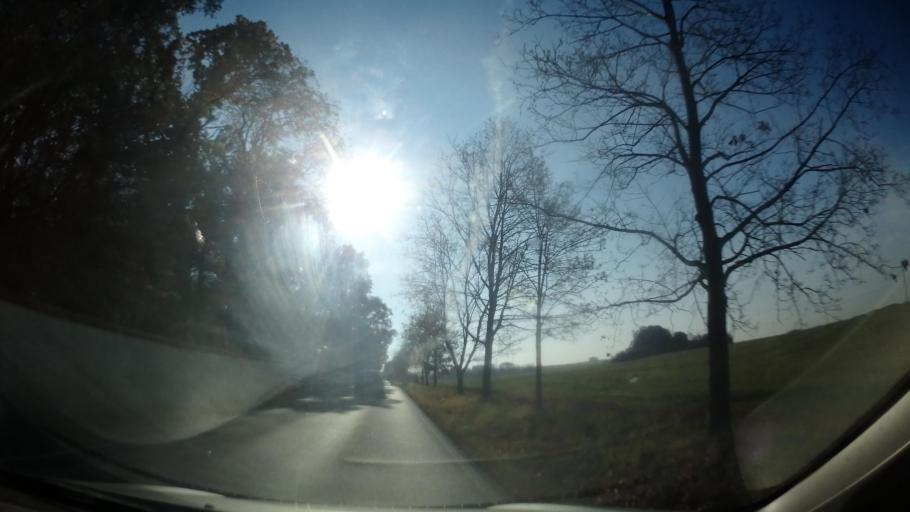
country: CZ
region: Praha
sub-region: Praha 20
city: Horni Pocernice
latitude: 50.0613
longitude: 14.6279
